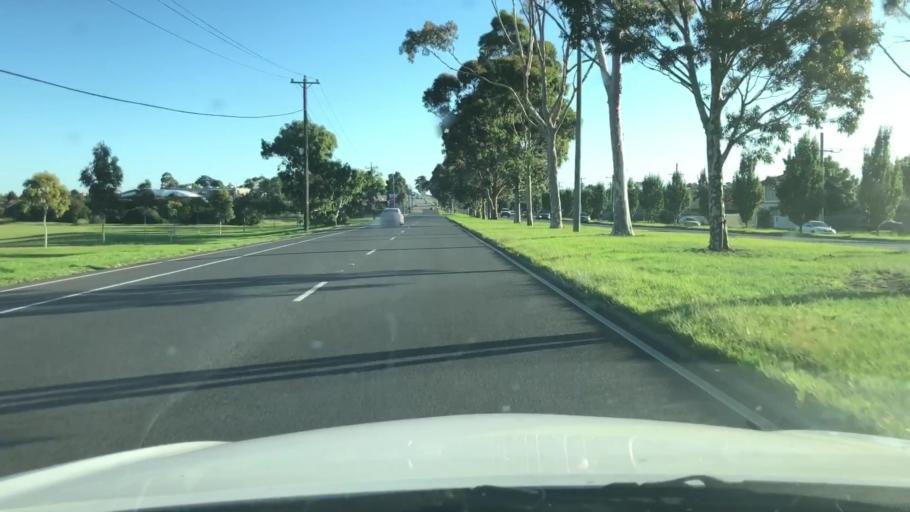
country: AU
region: Victoria
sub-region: Greater Dandenong
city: Dandenong North
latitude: -37.9656
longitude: 145.2244
